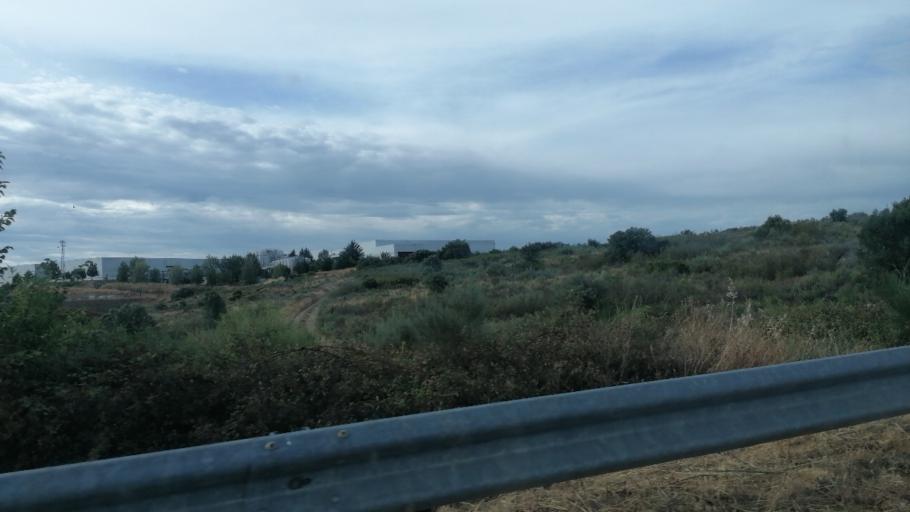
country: PT
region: Viseu
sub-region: Sao Joao da Pesqueira
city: Sao Joao da Pesqueira
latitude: 41.1146
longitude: -7.3873
